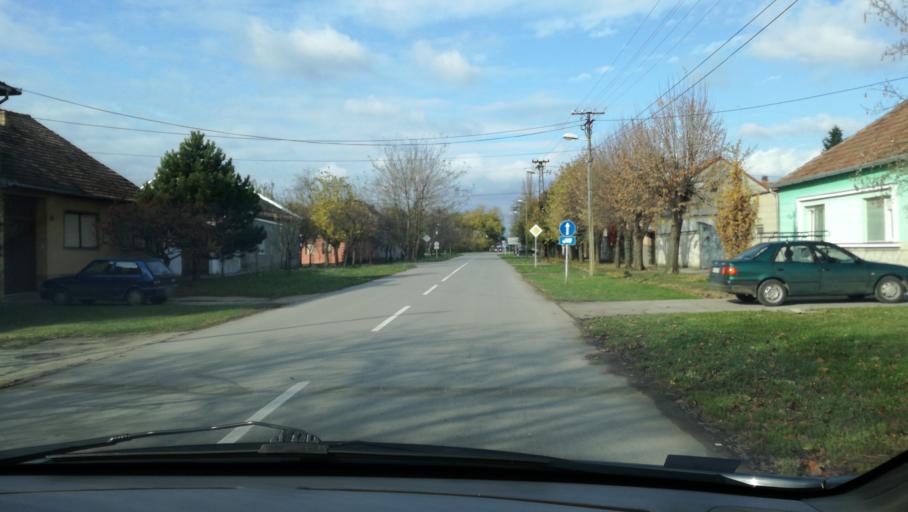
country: RS
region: Autonomna Pokrajina Vojvodina
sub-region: Severnobanatski Okrug
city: Kikinda
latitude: 45.8370
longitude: 20.4550
